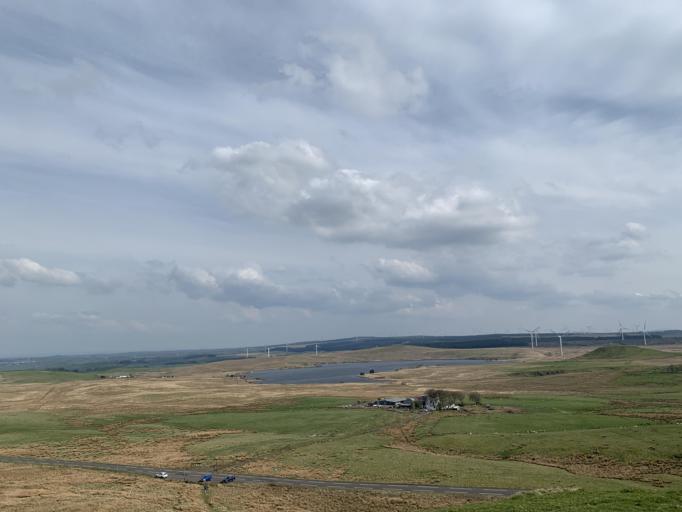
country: GB
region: Scotland
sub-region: East Renfrewshire
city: Newton Mearns
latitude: 55.7217
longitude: -4.3300
